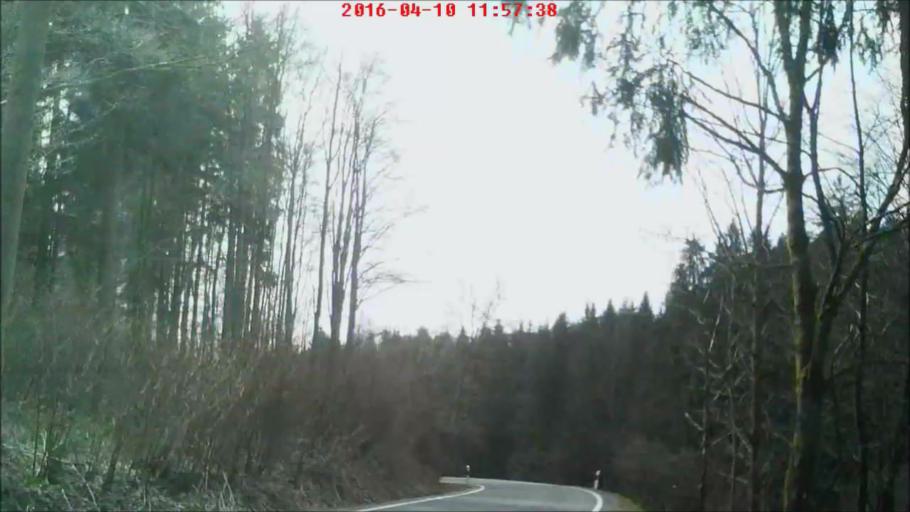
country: DE
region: Thuringia
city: Zella-Mehlis
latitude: 50.6801
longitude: 10.6489
